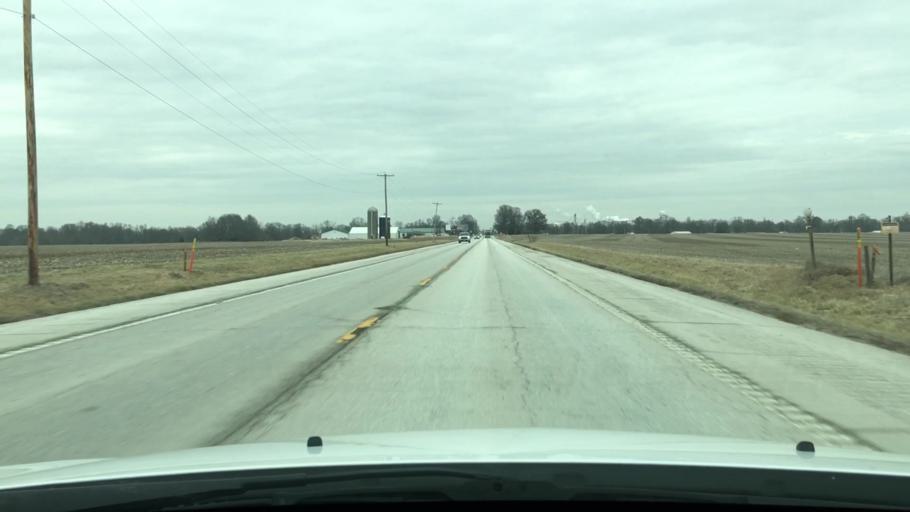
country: US
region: Missouri
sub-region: Montgomery County
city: Wellsville
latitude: 39.2294
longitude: -91.6460
